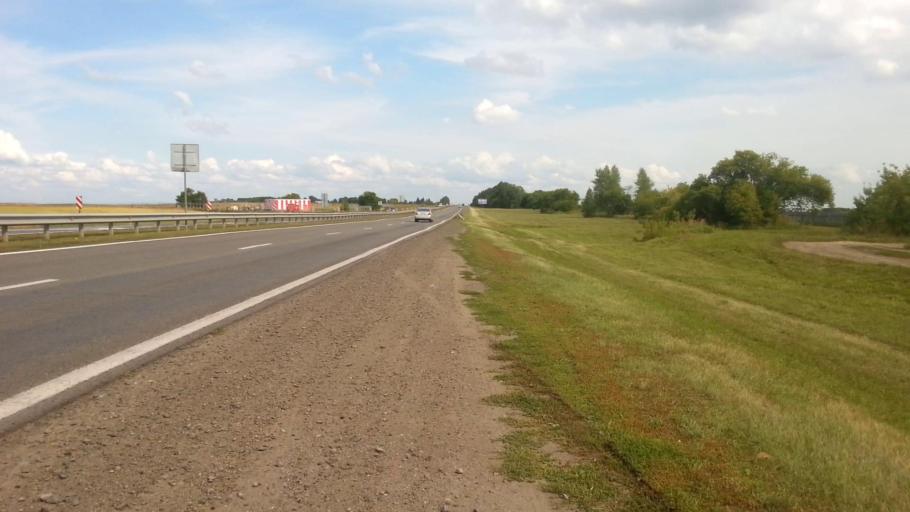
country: RU
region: Altai Krai
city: Nauchnyy Gorodok
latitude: 53.3564
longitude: 83.5097
